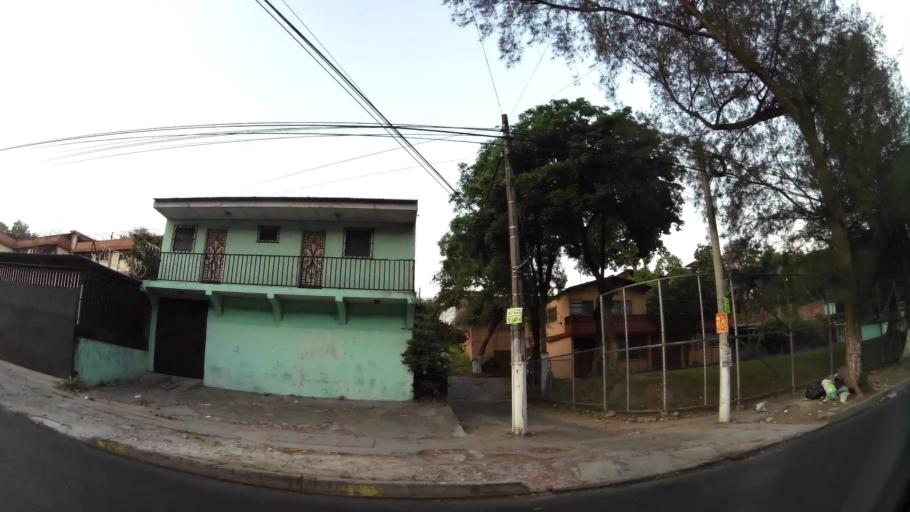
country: SV
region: San Salvador
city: Delgado
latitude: 13.7090
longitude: -89.1793
